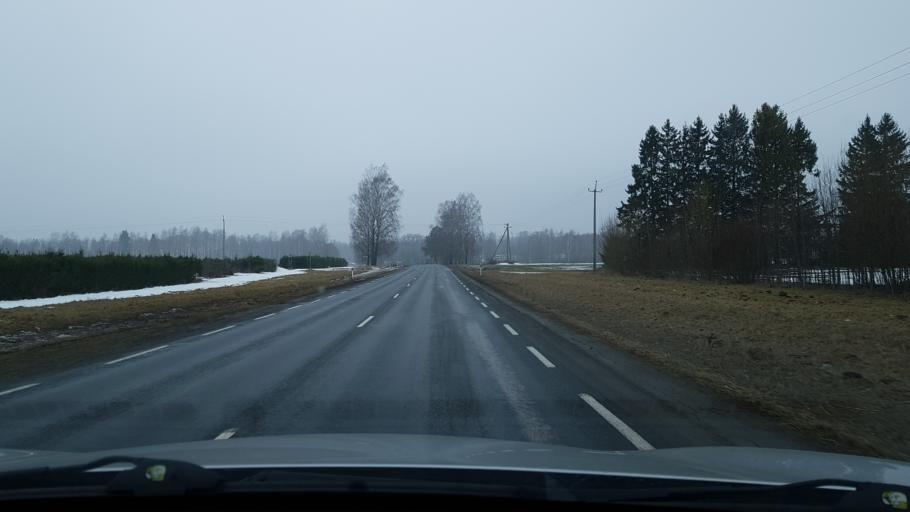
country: EE
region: Viljandimaa
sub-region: Viiratsi vald
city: Viiratsi
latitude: 58.2509
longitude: 25.8283
